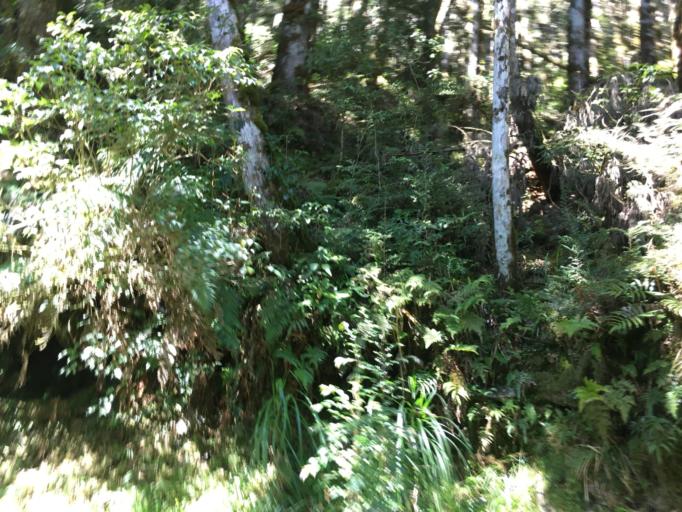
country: TW
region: Taiwan
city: Daxi
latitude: 24.5719
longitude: 121.4185
